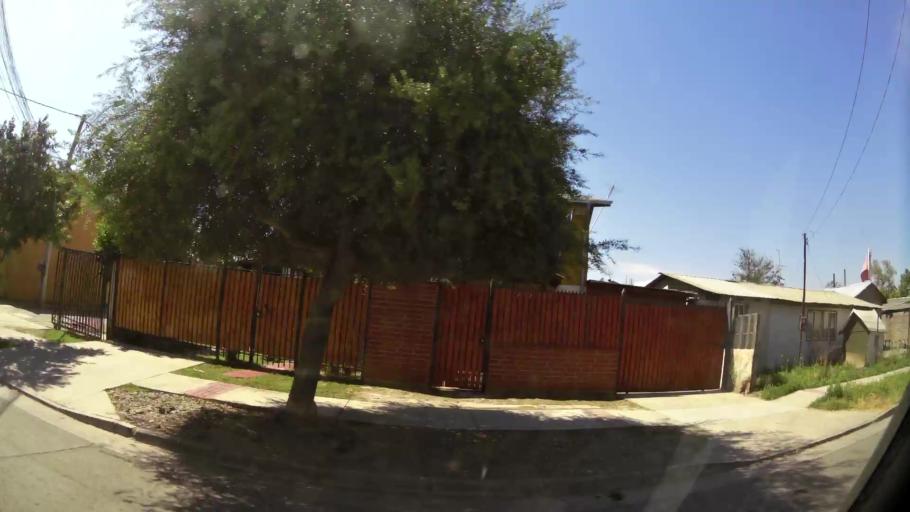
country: CL
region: Santiago Metropolitan
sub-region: Provincia de Talagante
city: Talagante
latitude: -33.6517
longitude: -70.9248
